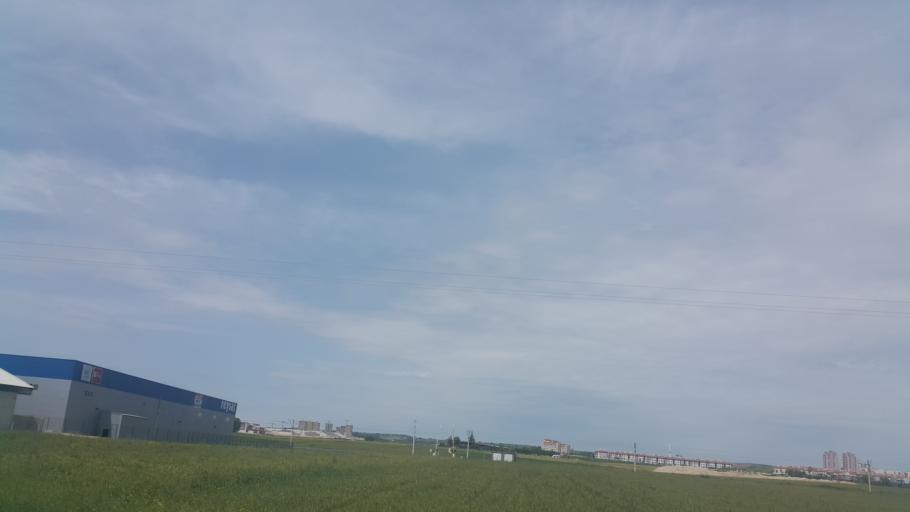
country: TR
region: Adana
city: Yakapinar
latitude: 36.9684
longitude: 35.5545
